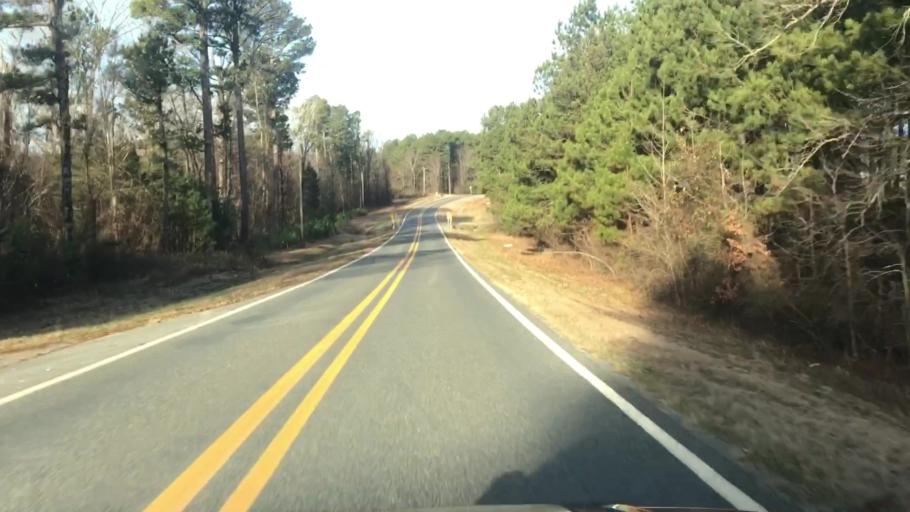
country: US
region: Arkansas
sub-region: Garland County
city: Rockwell
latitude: 34.4781
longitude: -93.2681
